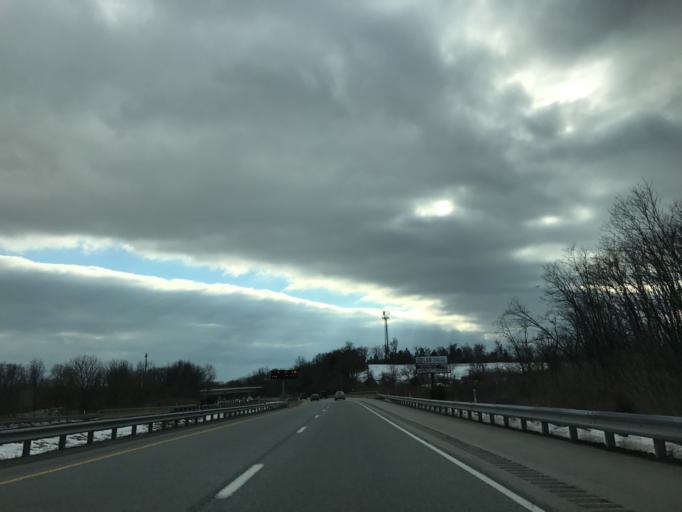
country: US
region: Pennsylvania
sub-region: York County
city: Shiloh
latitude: 39.9507
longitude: -76.7919
